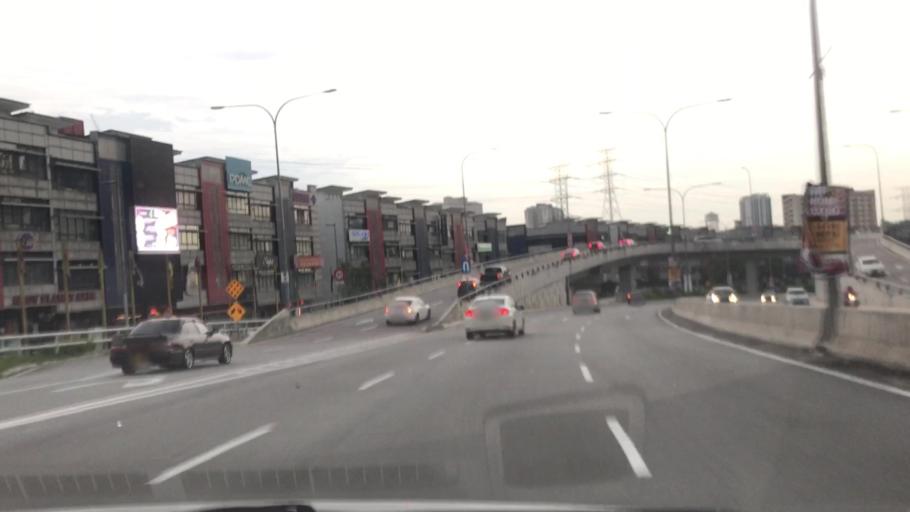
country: MY
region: Selangor
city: Kampong Baharu Balakong
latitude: 3.0487
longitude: 101.6719
